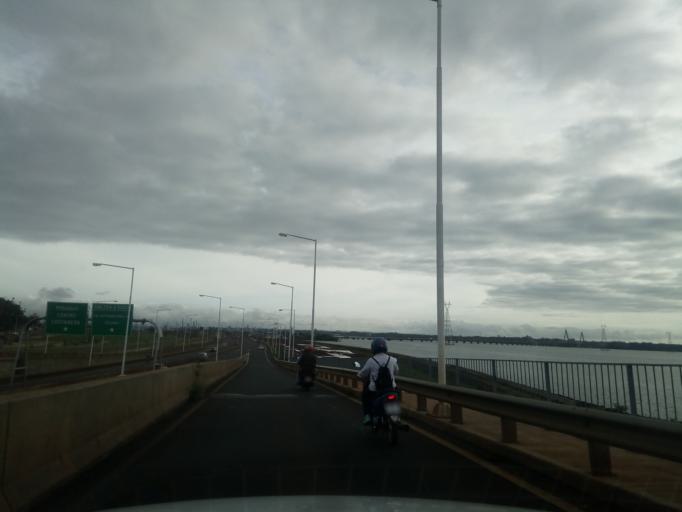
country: AR
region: Misiones
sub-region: Departamento de Capital
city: Posadas
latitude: -27.3843
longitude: -55.8840
